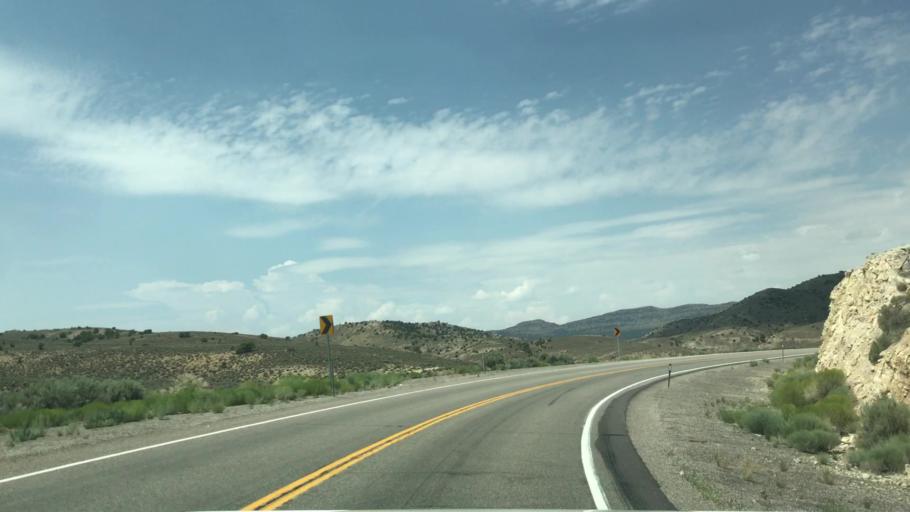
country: US
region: Nevada
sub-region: White Pine County
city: Ely
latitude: 39.3517
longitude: -115.3639
